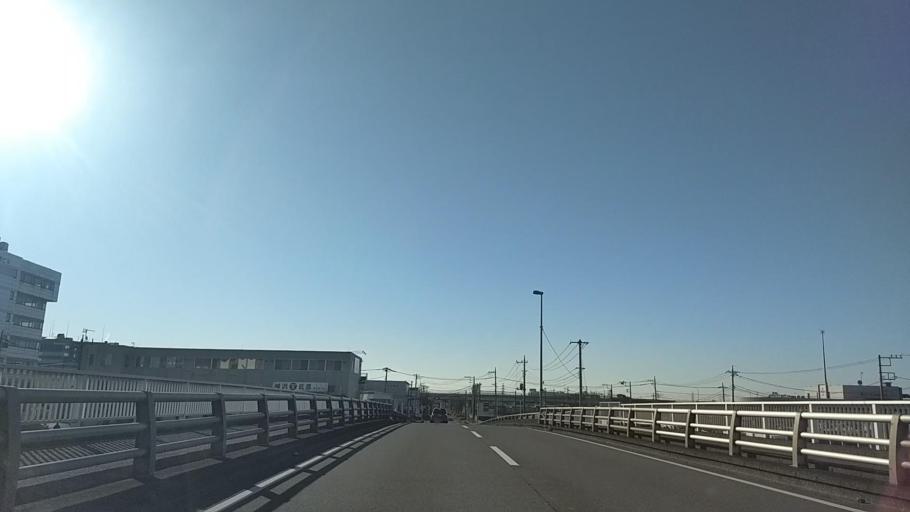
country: JP
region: Kanagawa
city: Atsugi
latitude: 35.4230
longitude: 139.3553
